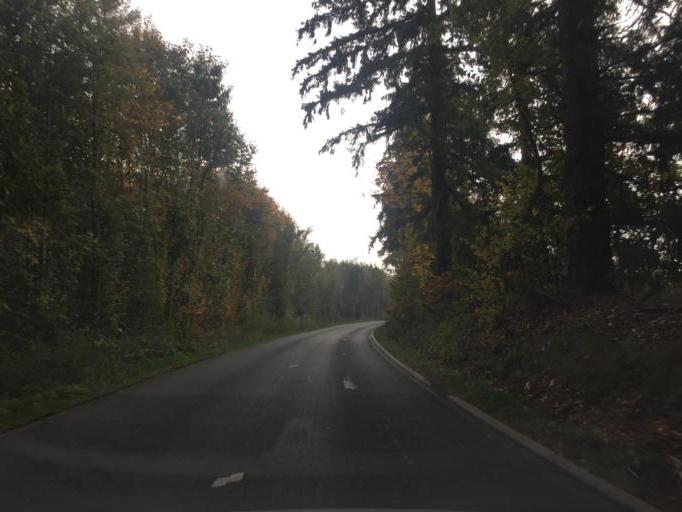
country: FR
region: Rhone-Alpes
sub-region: Departement de l'Ain
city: Tramoyes
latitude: 45.8951
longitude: 4.9702
